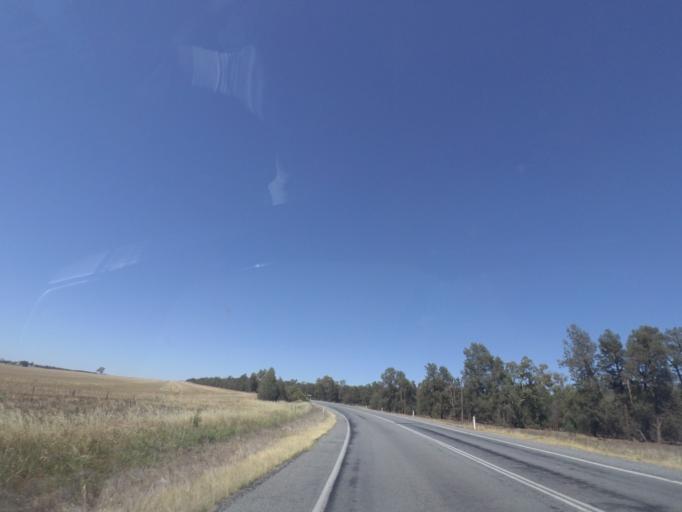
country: AU
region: New South Wales
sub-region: Narrandera
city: Narrandera
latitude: -34.4205
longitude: 146.8461
